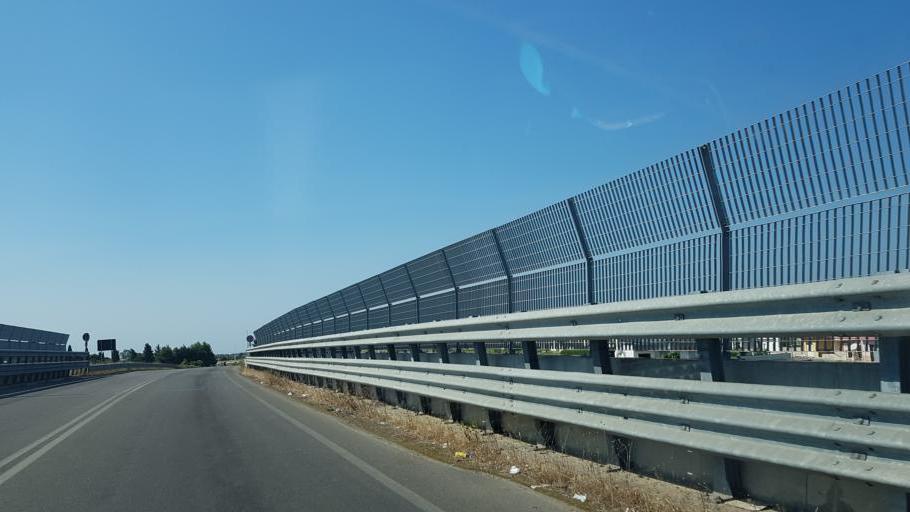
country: IT
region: Apulia
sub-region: Provincia di Lecce
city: Salice Salentino
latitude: 40.3883
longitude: 17.9696
